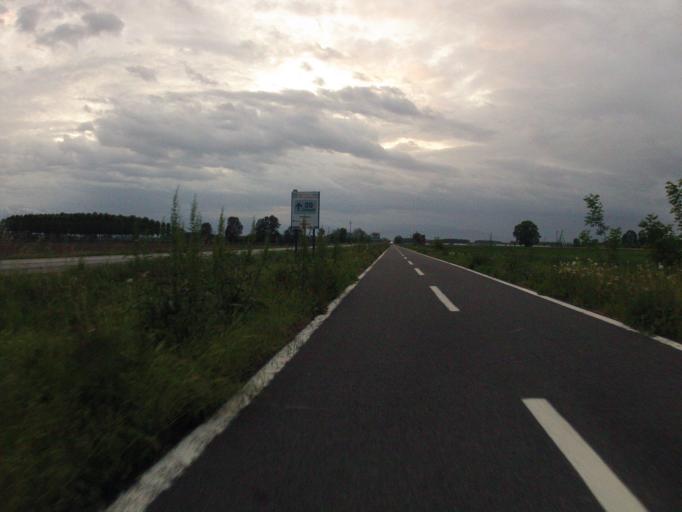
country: IT
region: Piedmont
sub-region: Provincia di Cuneo
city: Moretta
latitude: 44.7696
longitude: 7.5275
